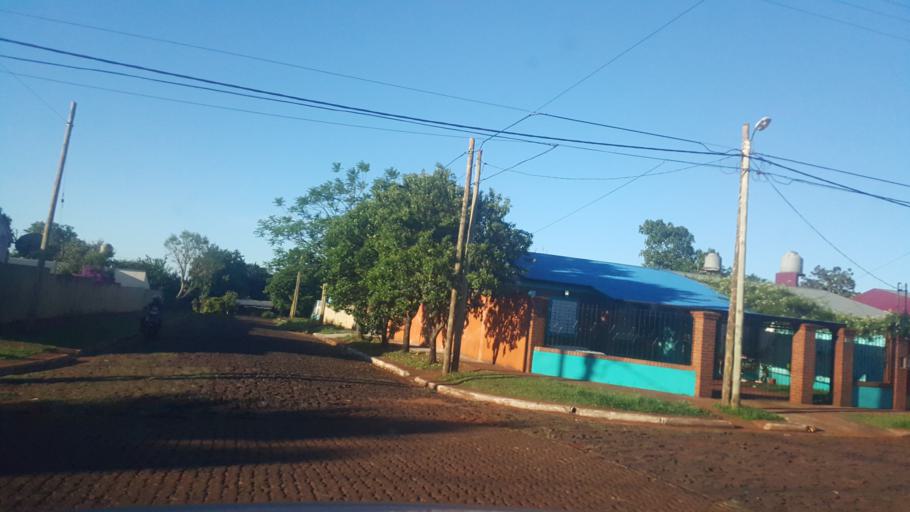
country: AR
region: Misiones
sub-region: Departamento de Capital
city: Posadas
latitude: -27.4237
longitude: -55.9486
